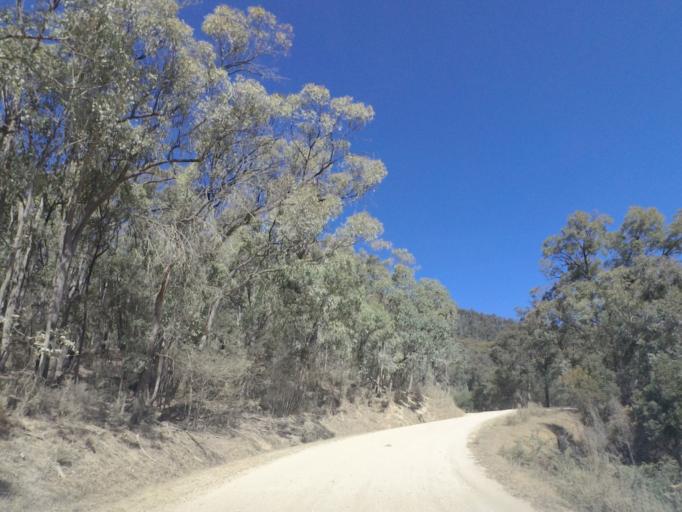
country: AU
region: Victoria
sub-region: Murrindindi
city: Alexandra
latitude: -37.3256
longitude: 145.8057
